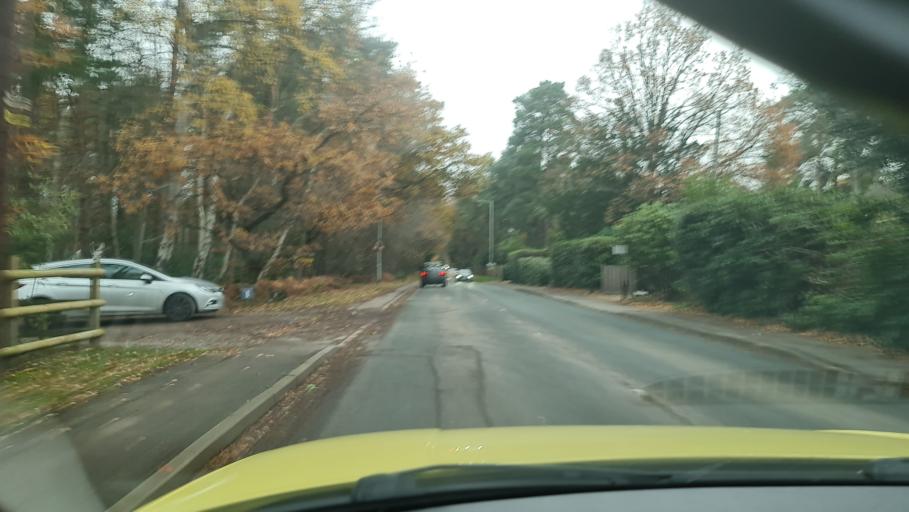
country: GB
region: England
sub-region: Hampshire
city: Yateley
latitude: 51.3718
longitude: -0.8248
